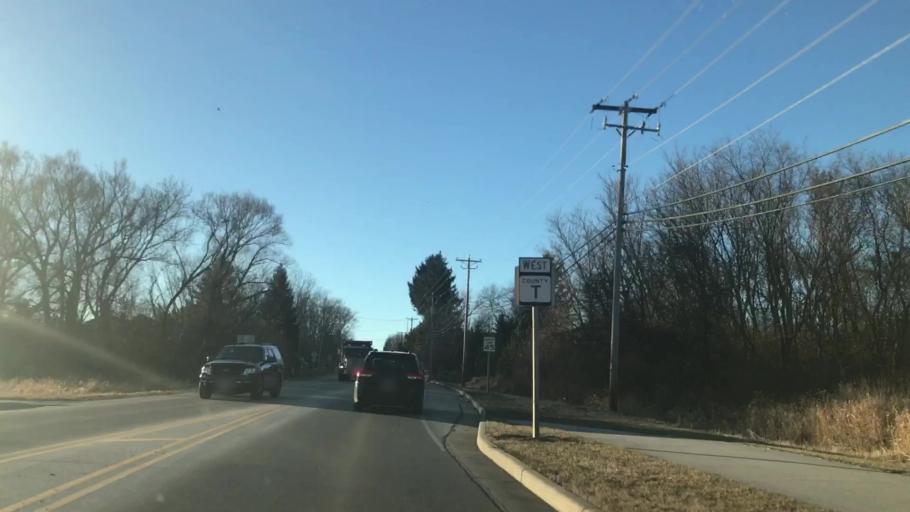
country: US
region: Wisconsin
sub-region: Ozaukee County
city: Cedarburg
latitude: 43.2935
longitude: -88.0053
